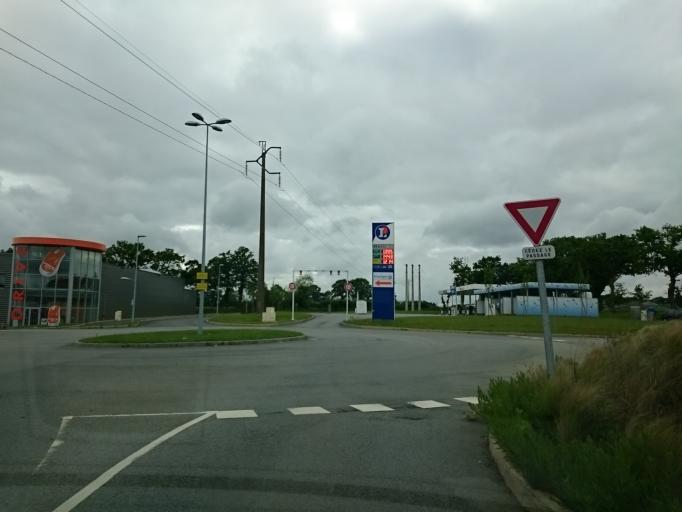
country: FR
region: Brittany
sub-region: Departement d'Ille-et-Vilaine
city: Chantepie
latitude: 48.0642
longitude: -1.6254
